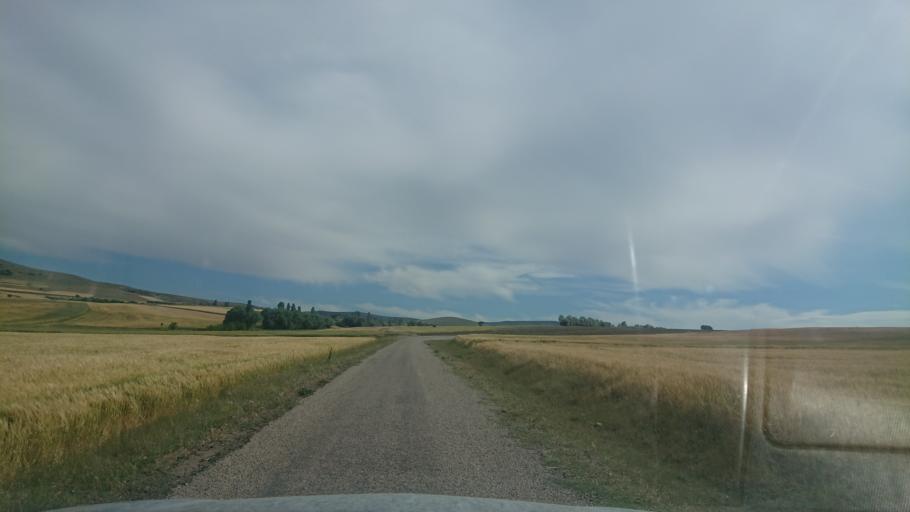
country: TR
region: Aksaray
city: Ortakoy
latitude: 38.8181
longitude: 34.0030
